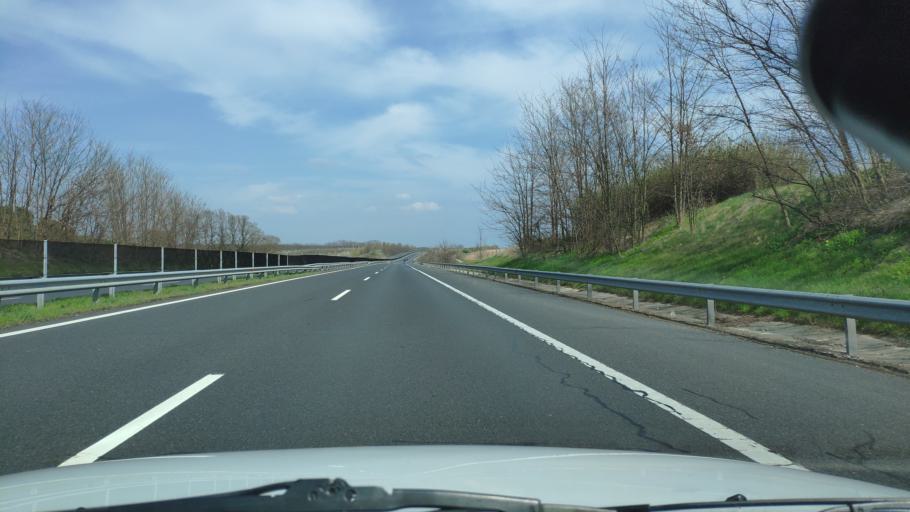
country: HU
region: Zala
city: Nagykanizsa
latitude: 46.4815
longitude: 17.0844
